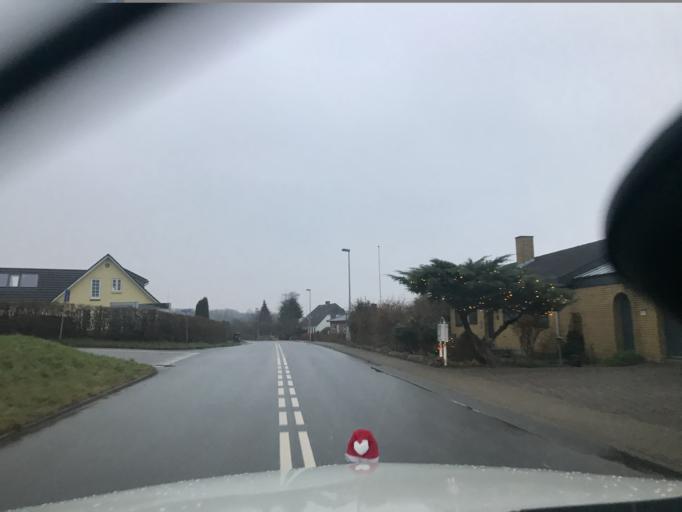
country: DK
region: South Denmark
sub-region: Sonderborg Kommune
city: Grasten
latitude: 54.8993
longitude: 9.5678
